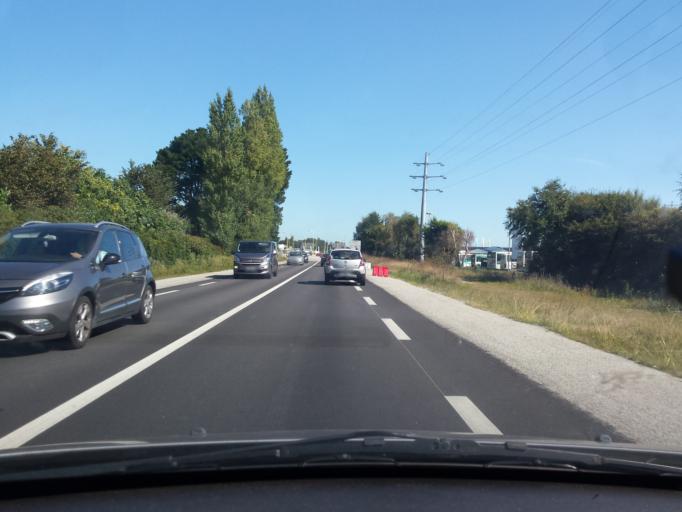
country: FR
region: Brittany
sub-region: Departement du Morbihan
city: Vannes
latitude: 47.6814
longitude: -2.7691
